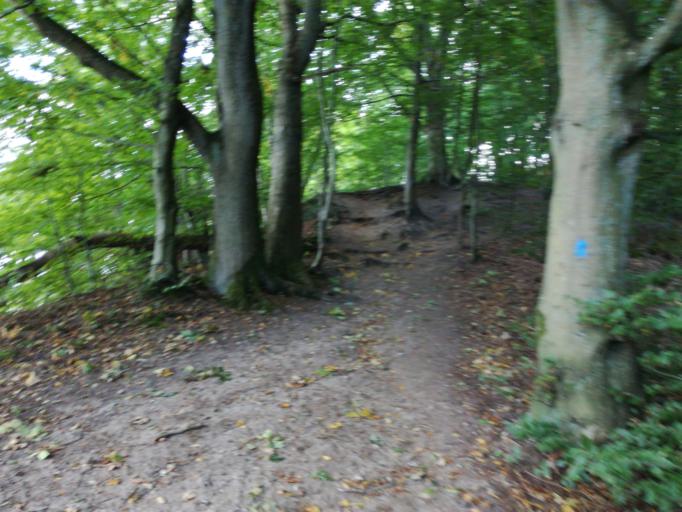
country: DK
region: South Denmark
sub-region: Fredericia Kommune
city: Snoghoj
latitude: 55.5150
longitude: 9.7038
